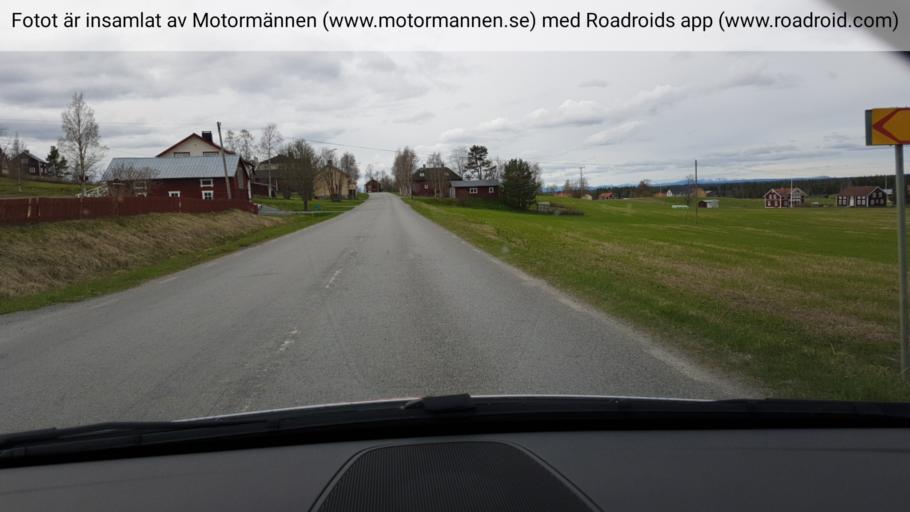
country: SE
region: Jaemtland
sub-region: Stroemsunds Kommun
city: Stroemsund
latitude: 63.6255
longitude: 15.2449
